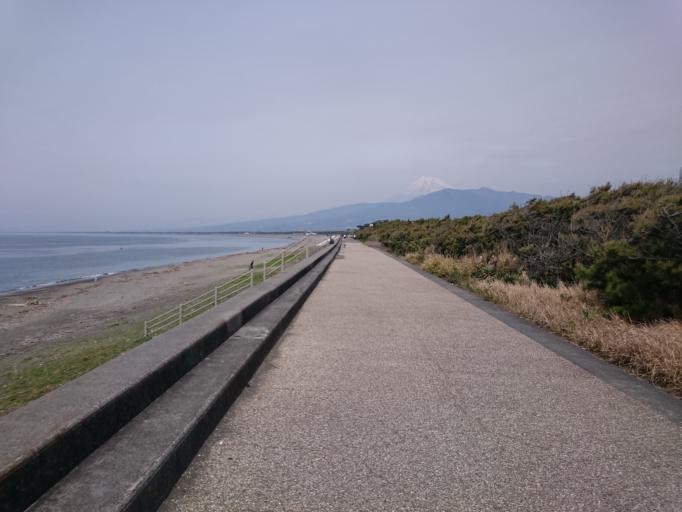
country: JP
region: Shizuoka
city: Numazu
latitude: 35.0874
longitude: 138.8511
